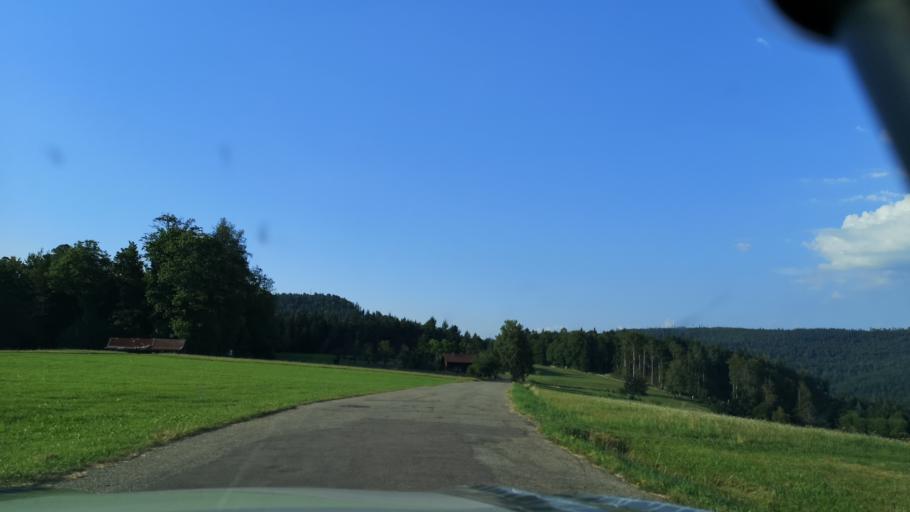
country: DE
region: Baden-Wuerttemberg
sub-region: Karlsruhe Region
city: Bad Herrenalb
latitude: 48.7688
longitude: 8.4406
